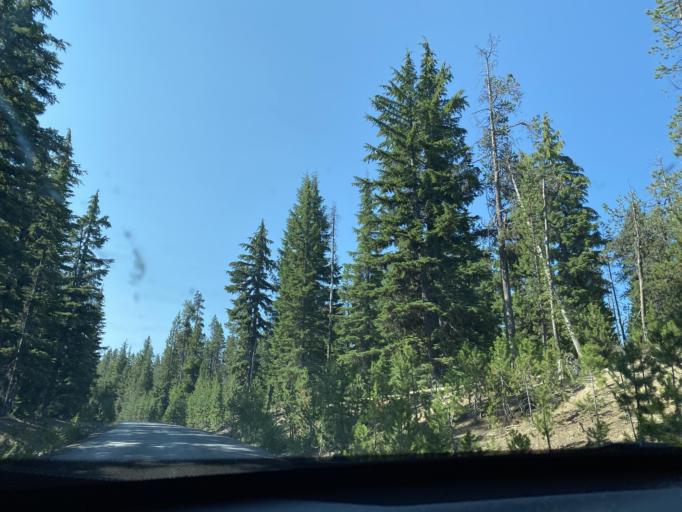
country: US
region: Oregon
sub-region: Deschutes County
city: Three Rivers
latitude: 43.7065
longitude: -121.2753
